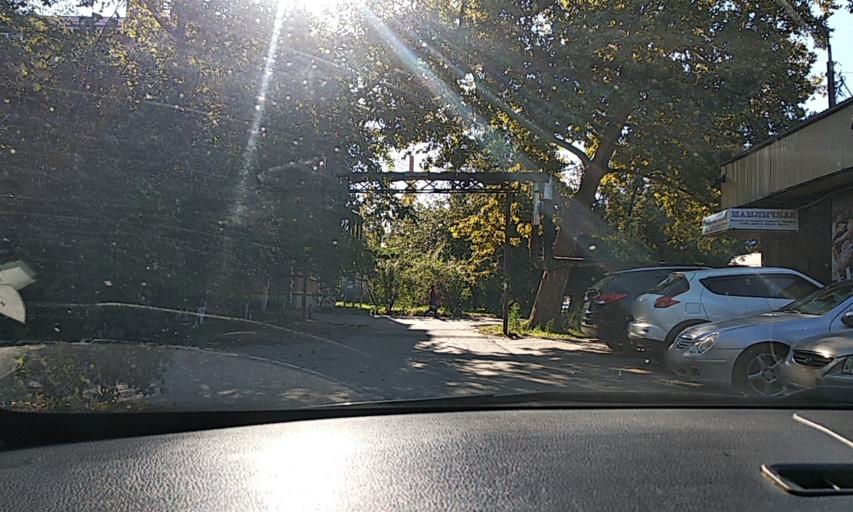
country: RU
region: Krasnodarskiy
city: Pashkovskiy
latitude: 45.0327
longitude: 39.1221
